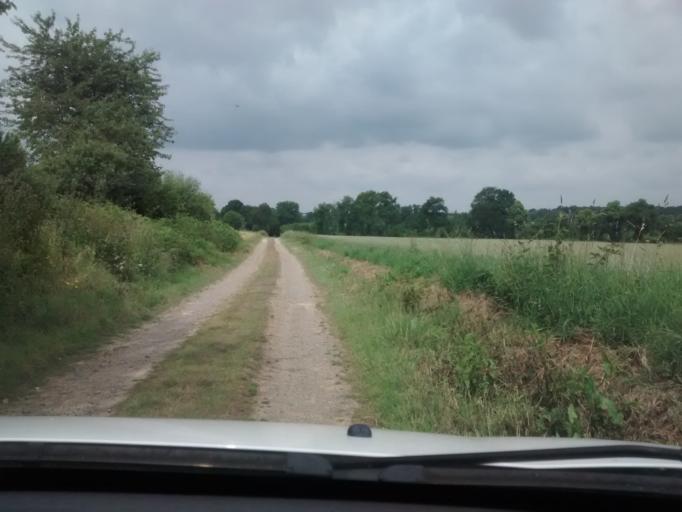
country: FR
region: Brittany
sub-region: Departement d'Ille-et-Vilaine
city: Servon-sur-Vilaine
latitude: 48.1442
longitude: -1.4715
